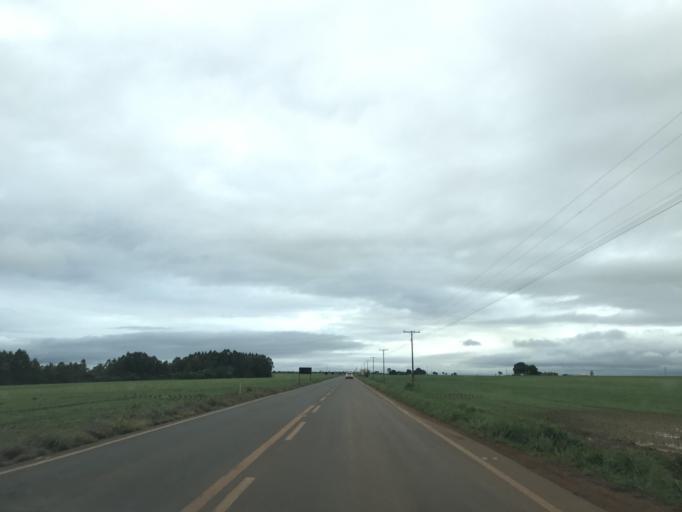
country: BR
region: Goias
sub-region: Luziania
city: Luziania
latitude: -16.3088
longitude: -48.0134
